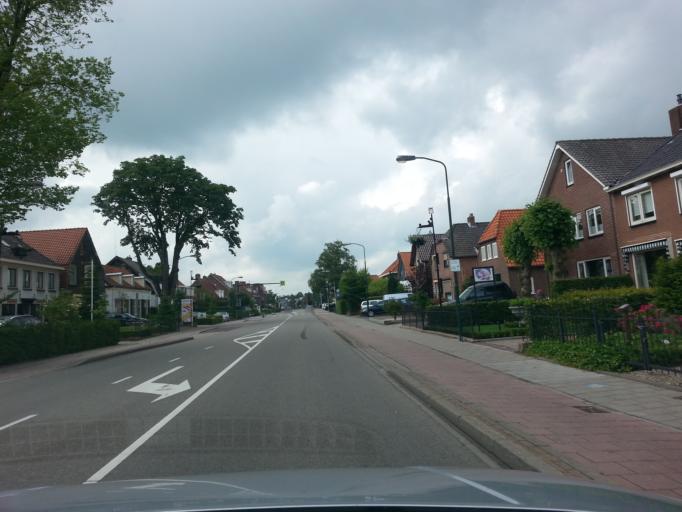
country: NL
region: Gelderland
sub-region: Gemeente Ede
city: Ederveen
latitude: 52.0736
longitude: 5.5408
